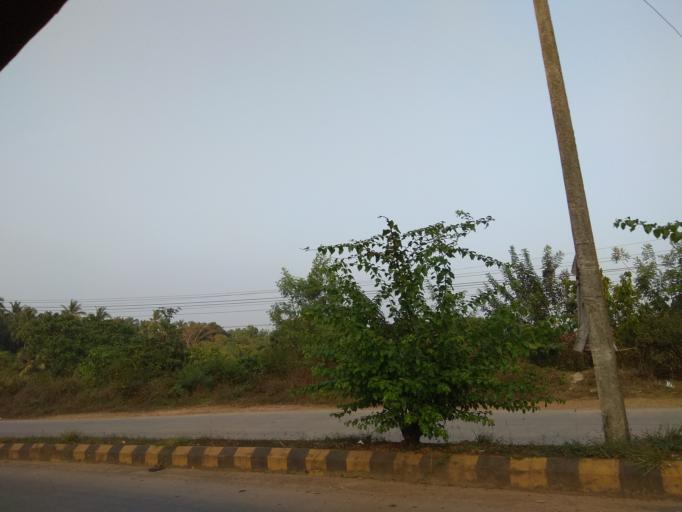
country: IN
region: Karnataka
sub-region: Dakshina Kannada
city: Mangalore
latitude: 12.9287
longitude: 74.8593
